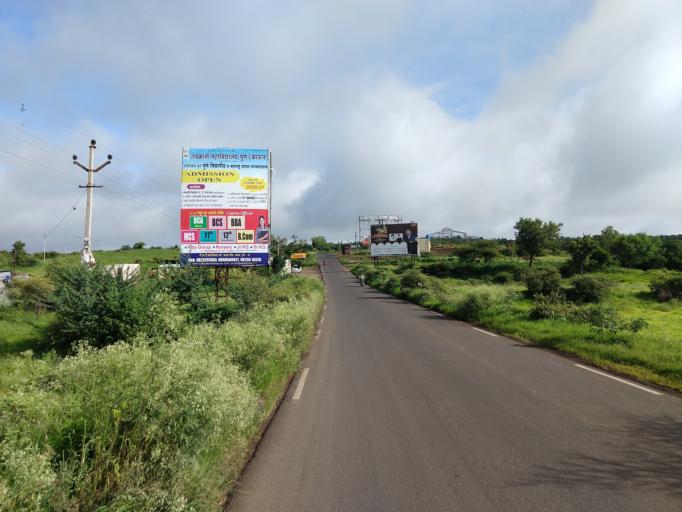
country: IN
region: Maharashtra
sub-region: Pune Division
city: Khed
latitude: 18.3975
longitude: 73.9144
